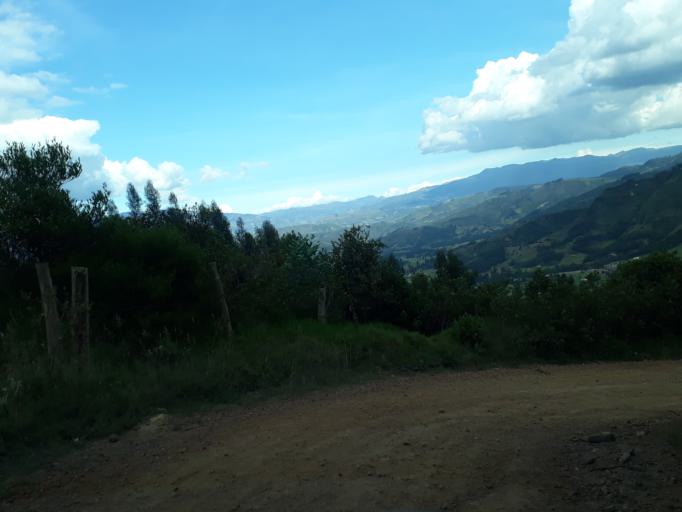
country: CO
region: Boyaca
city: Santa Rosa de Viterbo
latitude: 5.8642
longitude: -72.9679
